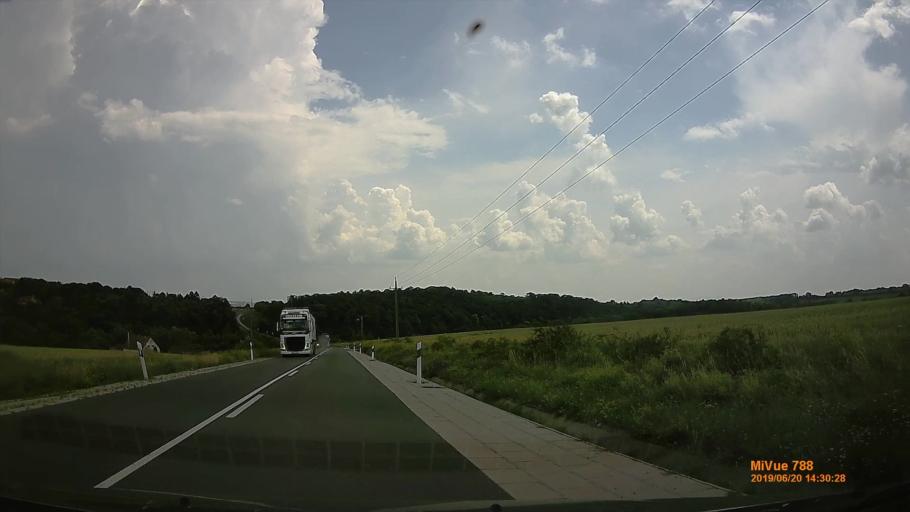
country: HU
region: Baranya
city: Hosszuheteny
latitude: 46.1488
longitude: 18.3453
